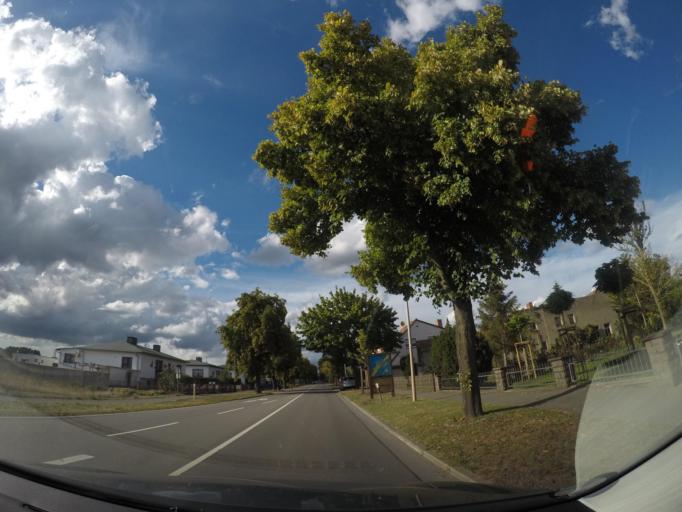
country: DE
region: Saxony-Anhalt
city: Bulstringen
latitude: 52.3169
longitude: 11.3499
